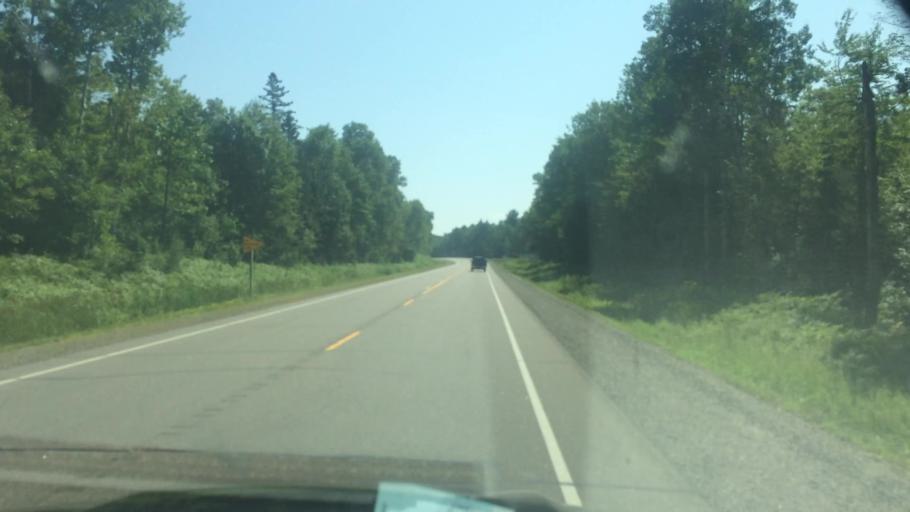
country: US
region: Wisconsin
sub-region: Lincoln County
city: Tomahawk
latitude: 45.5679
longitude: -89.6261
